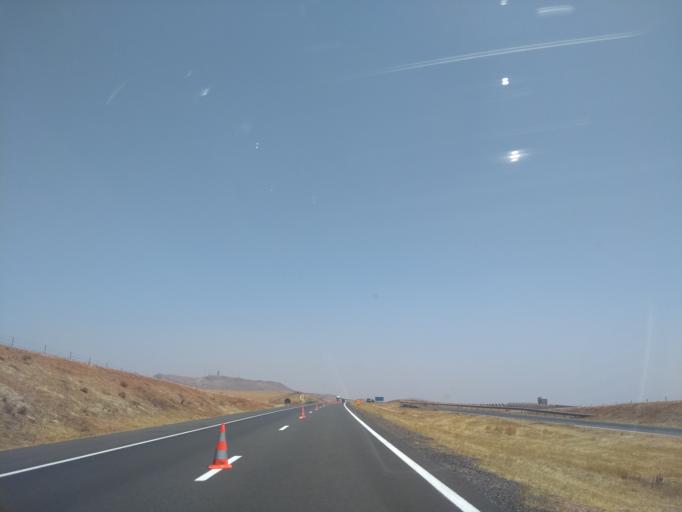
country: MA
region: Marrakech-Tensift-Al Haouz
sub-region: Kelaa-Des-Sraghna
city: Sidi Abdallah
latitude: 32.4419
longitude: -7.9319
